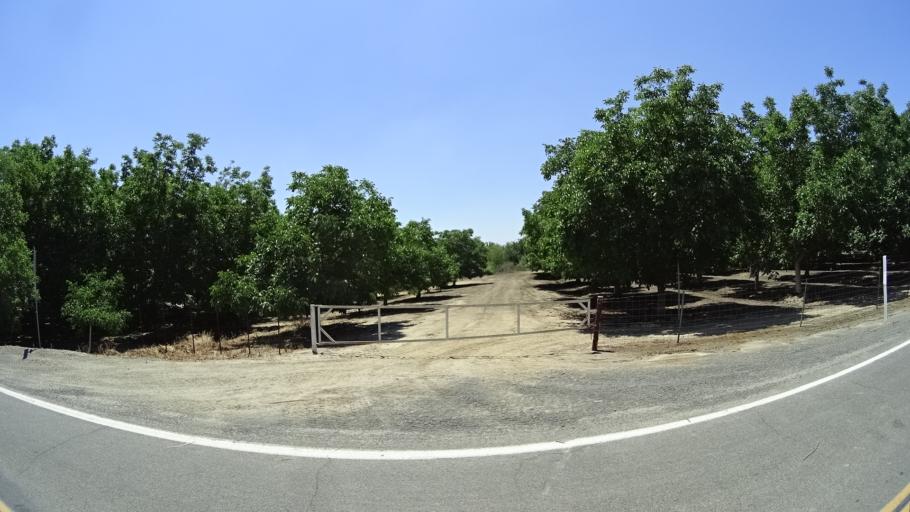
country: US
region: California
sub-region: Fresno County
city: Kingsburg
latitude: 36.4814
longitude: -119.5686
